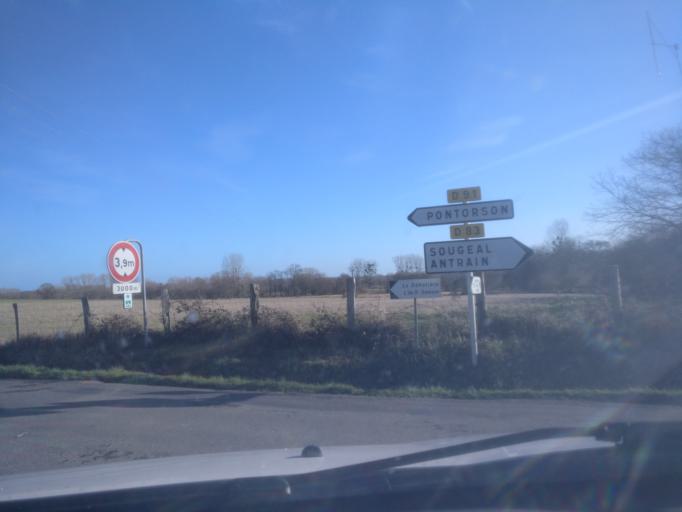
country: FR
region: Lower Normandy
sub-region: Departement de la Manche
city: Pontorson
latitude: 48.5299
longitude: -1.5245
